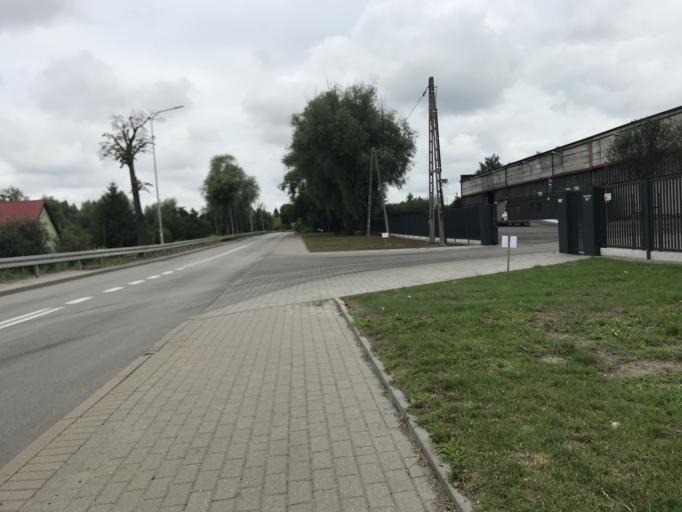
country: PL
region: Warmian-Masurian Voivodeship
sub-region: Powiat elblaski
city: Elblag
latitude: 54.1681
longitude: 19.3885
